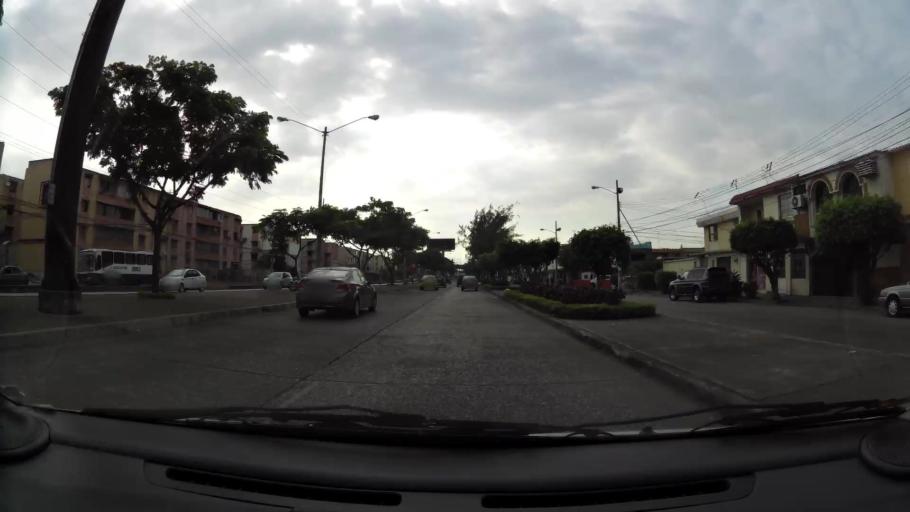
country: EC
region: Guayas
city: Eloy Alfaro
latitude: -2.1380
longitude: -79.8919
